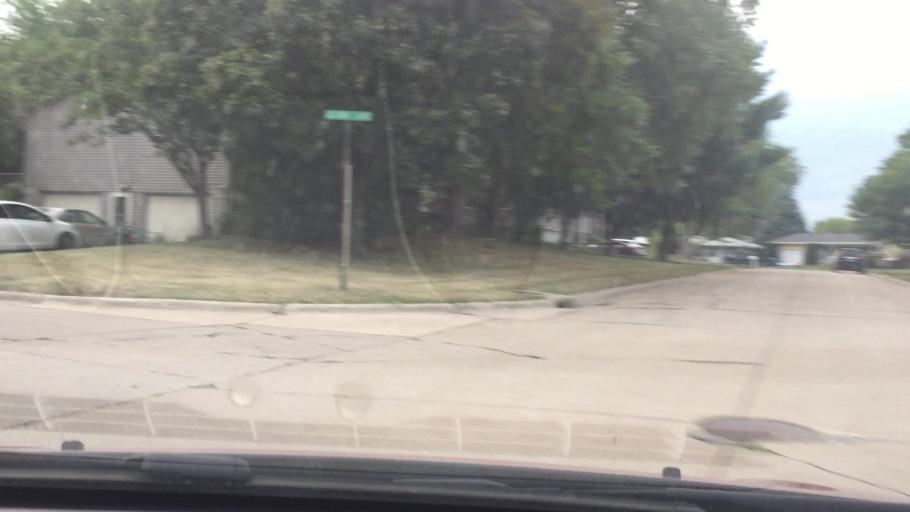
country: US
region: Iowa
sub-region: Muscatine County
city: Muscatine
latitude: 41.4425
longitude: -91.0516
